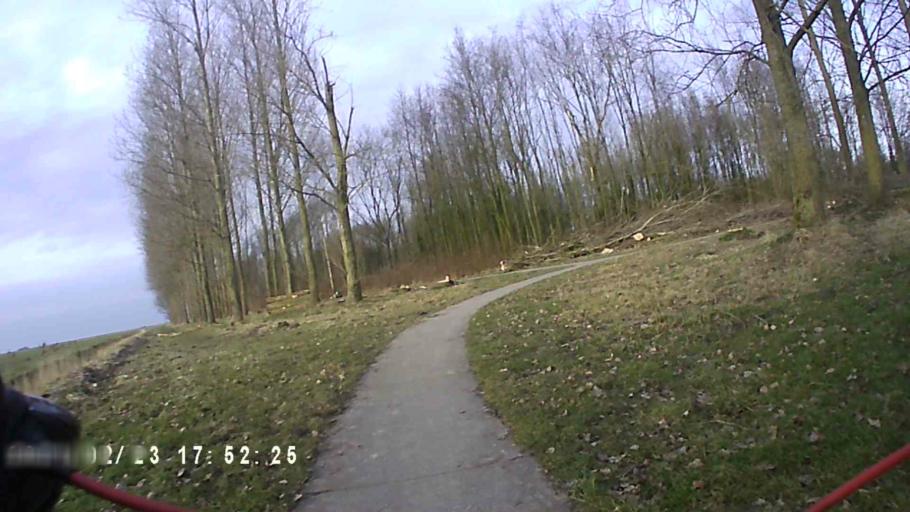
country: NL
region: Groningen
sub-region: Gemeente Winsum
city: Winsum
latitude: 53.3938
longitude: 6.5491
